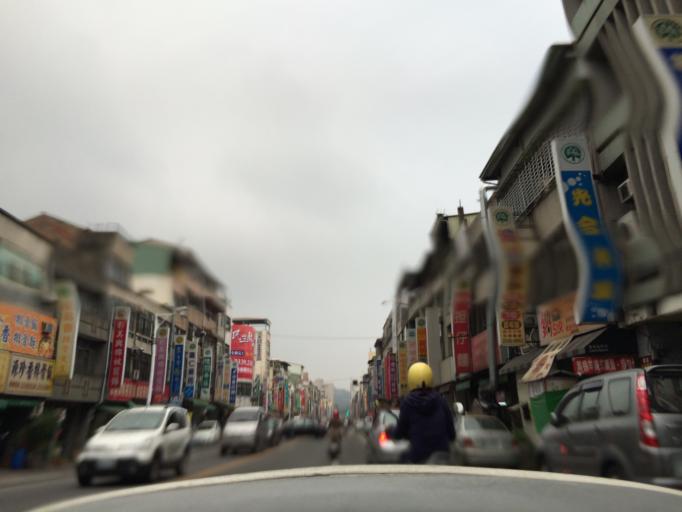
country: TW
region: Taiwan
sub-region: Taichung City
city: Taichung
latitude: 24.0678
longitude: 120.6990
